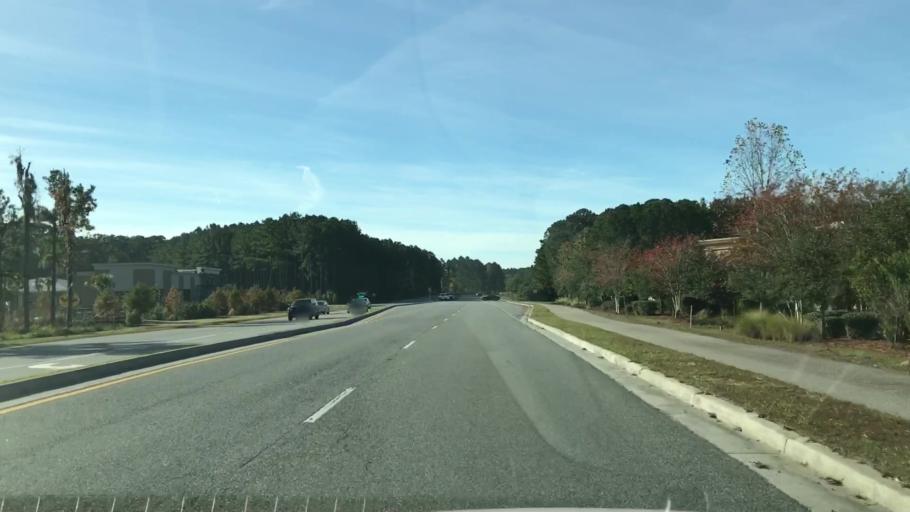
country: US
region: South Carolina
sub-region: Beaufort County
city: Bluffton
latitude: 32.2847
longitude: -80.9101
